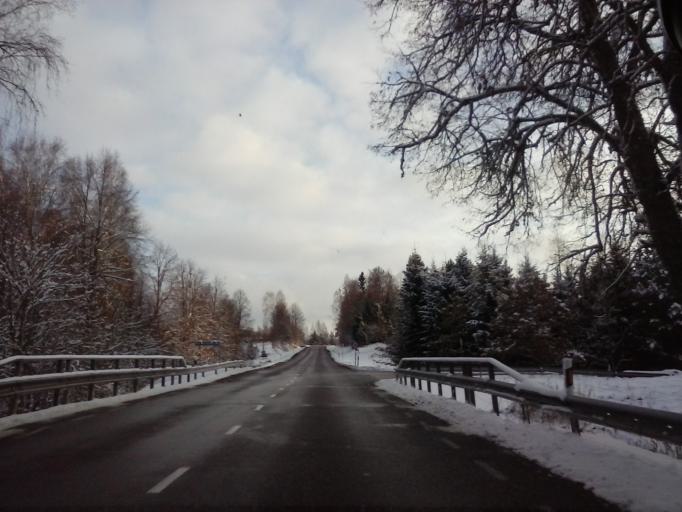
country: EE
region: Tartu
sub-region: Tartu linn
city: Tartu
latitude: 58.3505
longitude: 26.9101
